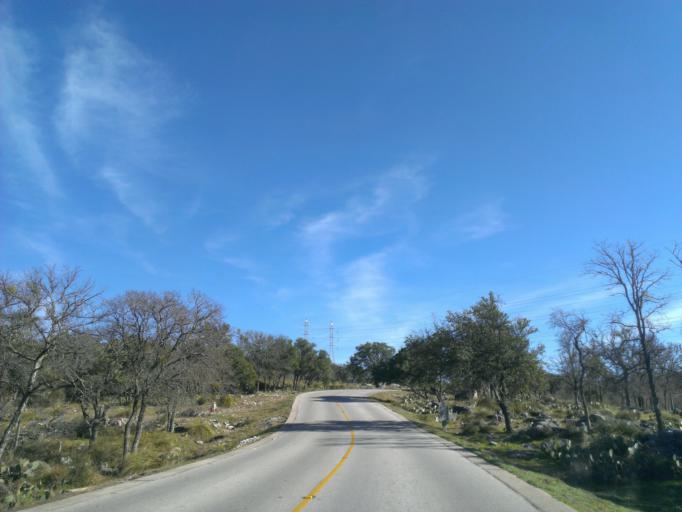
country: US
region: Texas
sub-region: Llano County
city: Horseshoe Bay
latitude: 30.5443
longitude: -98.3468
